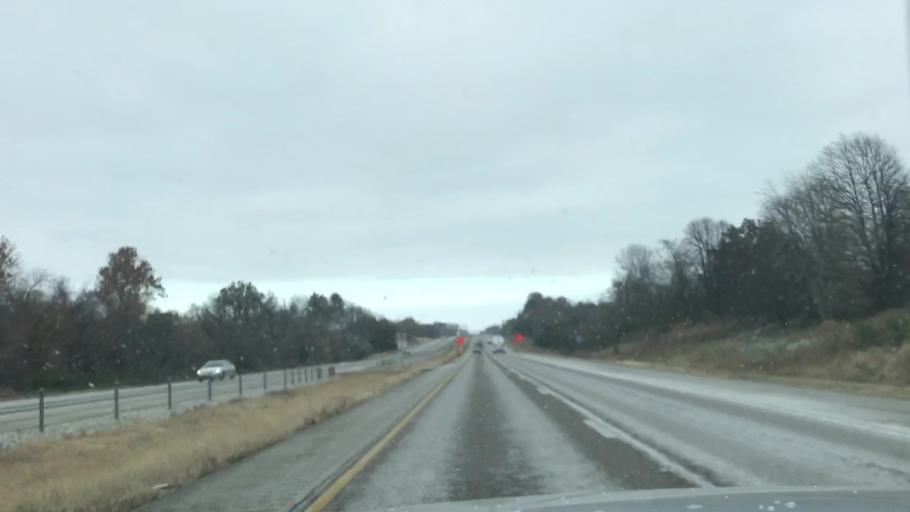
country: US
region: Illinois
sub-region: Madison County
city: Troy
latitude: 38.7636
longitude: -89.9039
